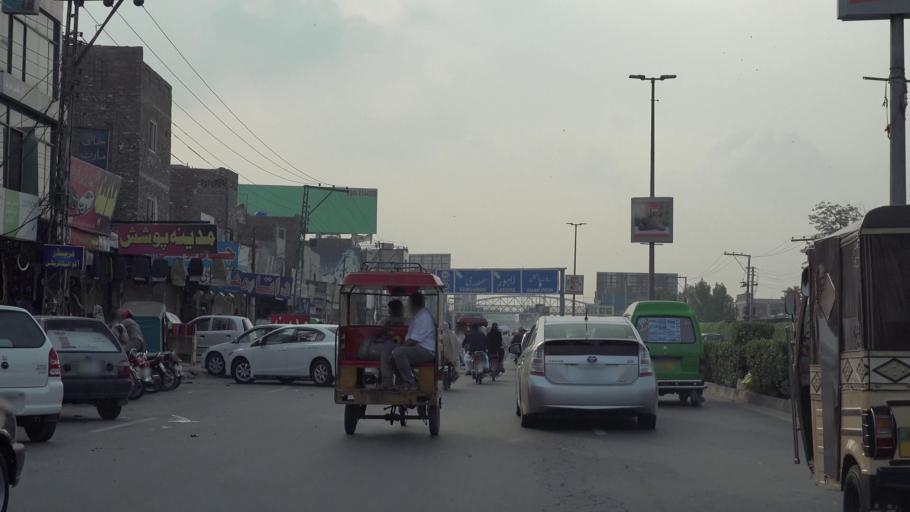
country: PK
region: Punjab
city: Faisalabad
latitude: 31.4182
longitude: 73.1066
